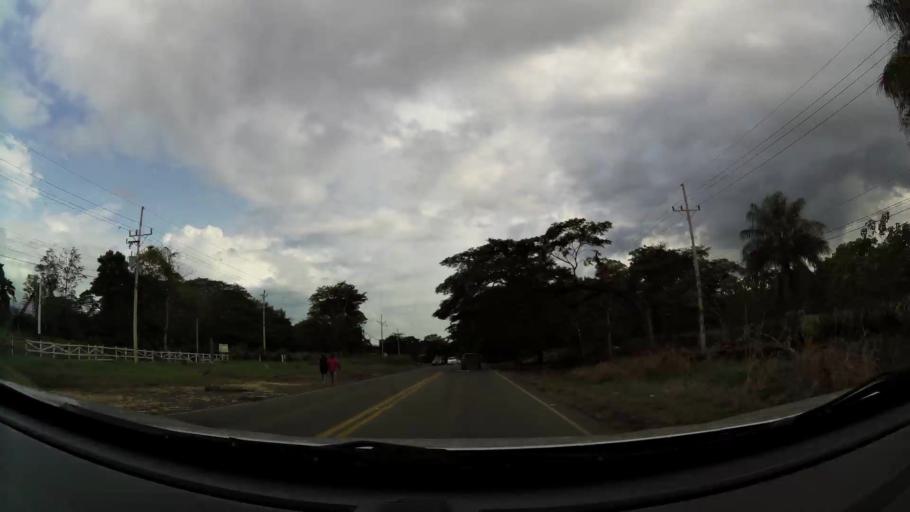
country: CR
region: Guanacaste
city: Juntas
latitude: 10.2619
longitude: -85.0182
